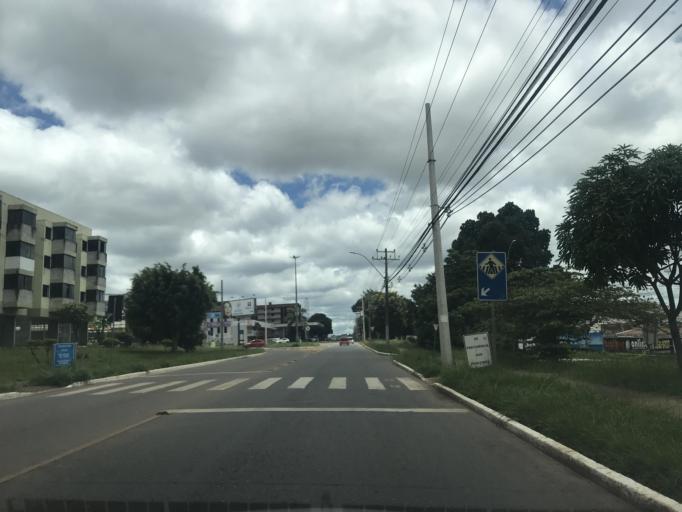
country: BR
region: Federal District
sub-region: Brasilia
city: Brasilia
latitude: -15.6526
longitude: -47.7902
